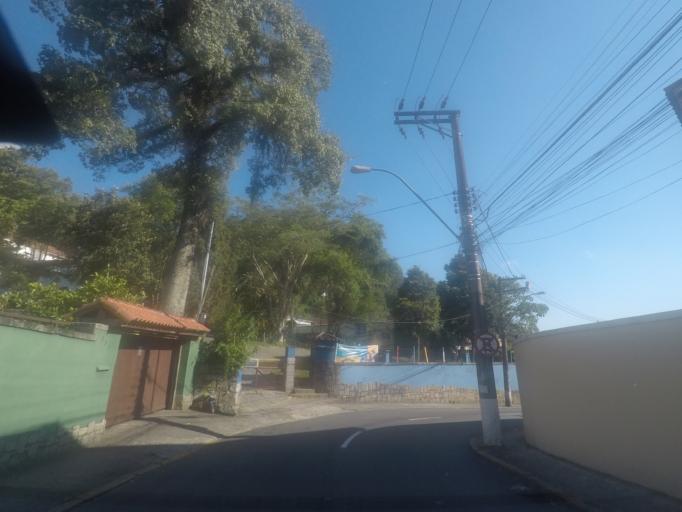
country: BR
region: Rio de Janeiro
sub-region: Petropolis
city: Petropolis
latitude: -22.5145
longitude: -43.1677
